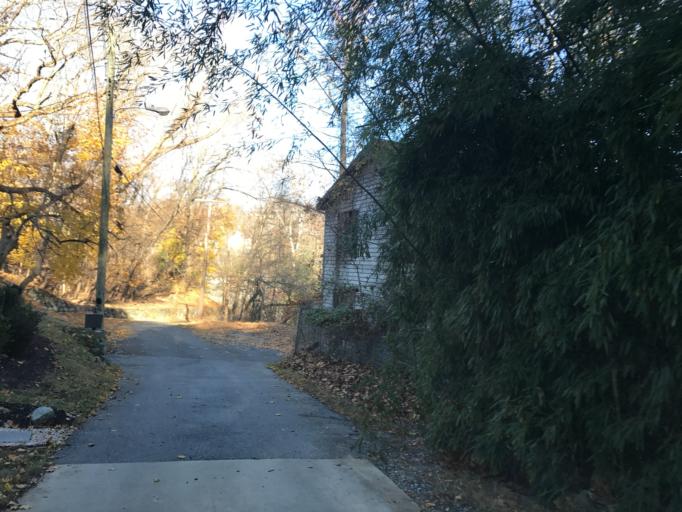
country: US
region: Maryland
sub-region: Howard County
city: Ellicott City
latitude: 39.2651
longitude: -76.7941
